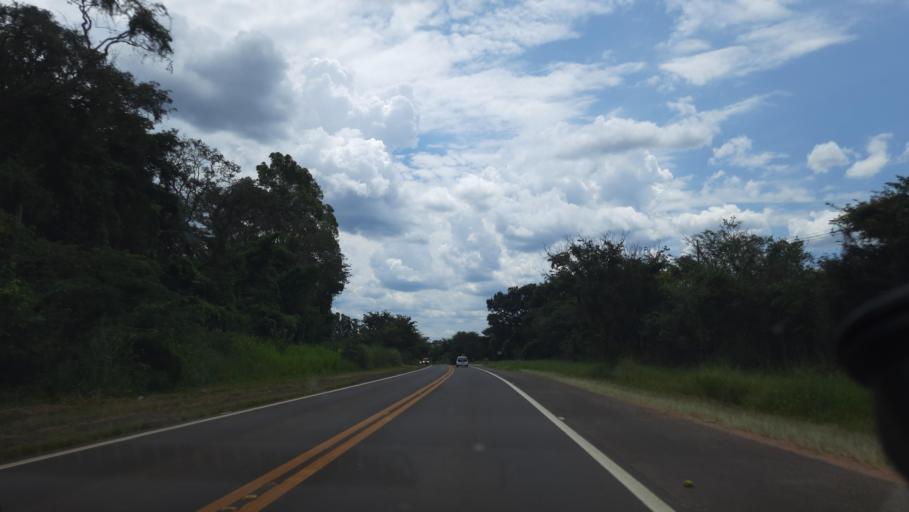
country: BR
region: Sao Paulo
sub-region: Mococa
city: Mococa
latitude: -21.4683
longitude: -47.0961
